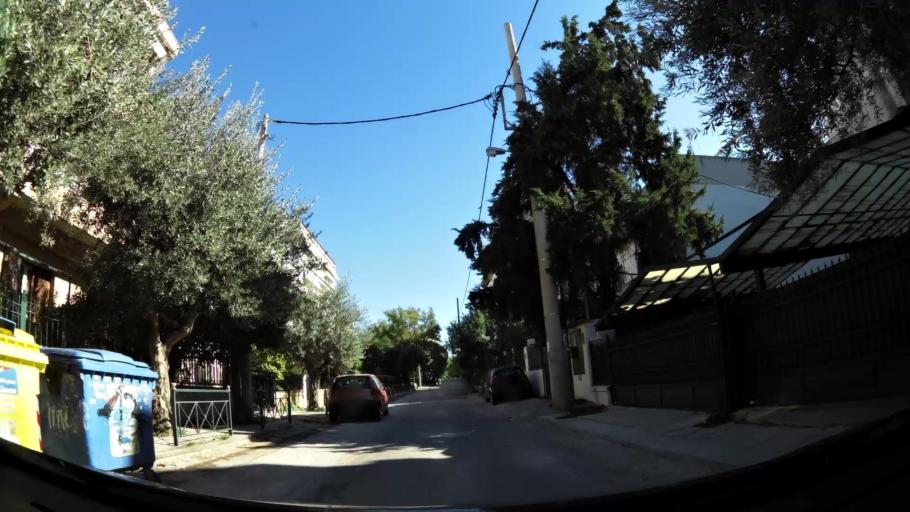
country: GR
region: Attica
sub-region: Nomarchia Athinas
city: Vrilissia
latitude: 38.0265
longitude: 23.8241
